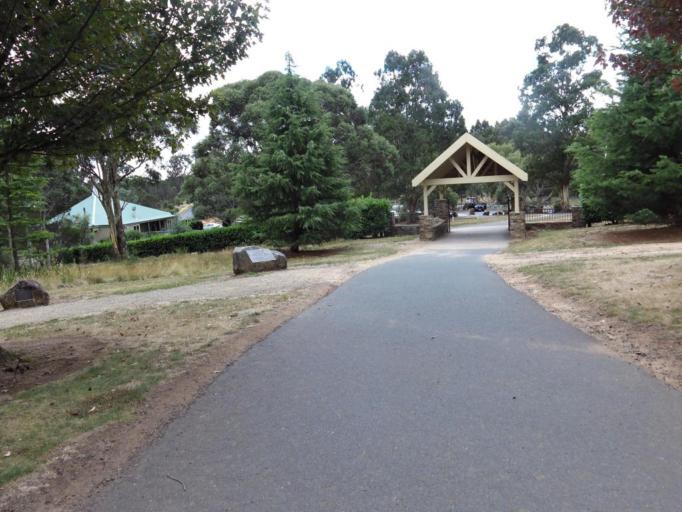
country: AU
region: Victoria
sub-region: Hume
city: Sunbury
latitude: -37.3871
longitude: 144.5763
